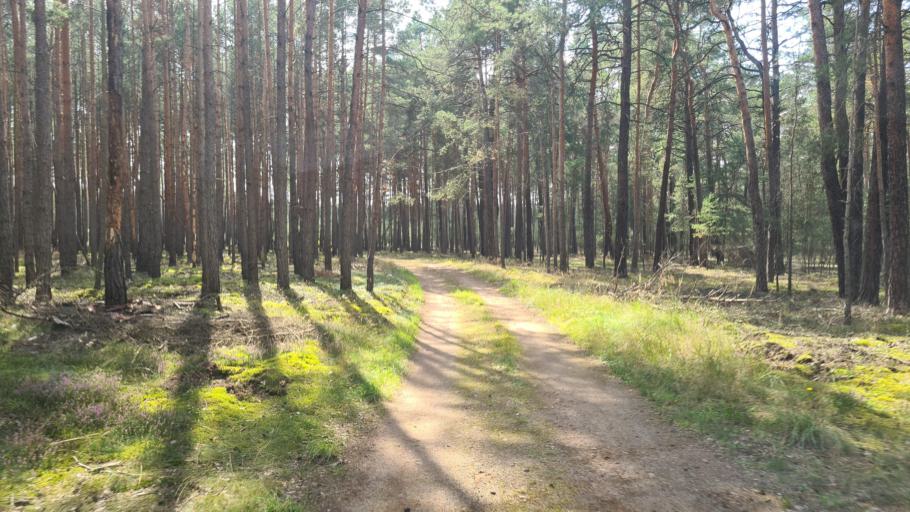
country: DE
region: Brandenburg
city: Schonewalde
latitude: 51.7542
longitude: 13.6017
